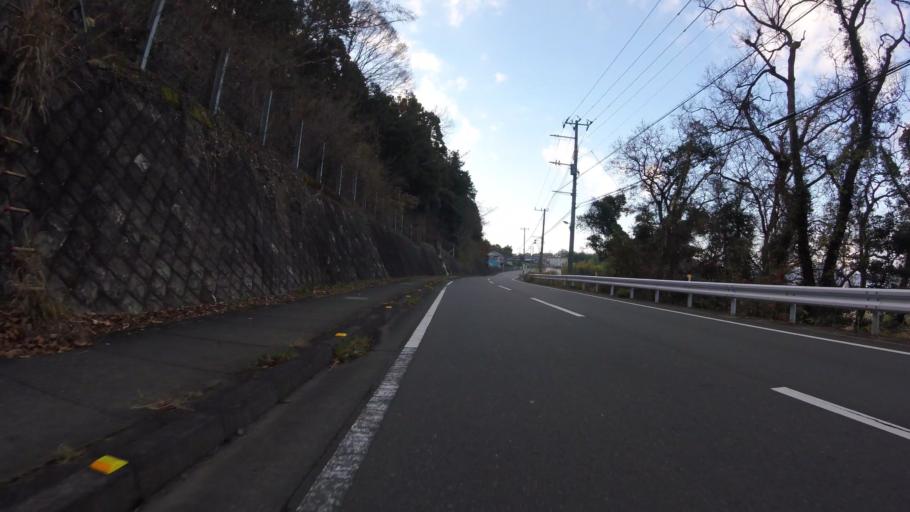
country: JP
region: Shizuoka
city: Mishima
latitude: 35.0990
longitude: 138.9634
